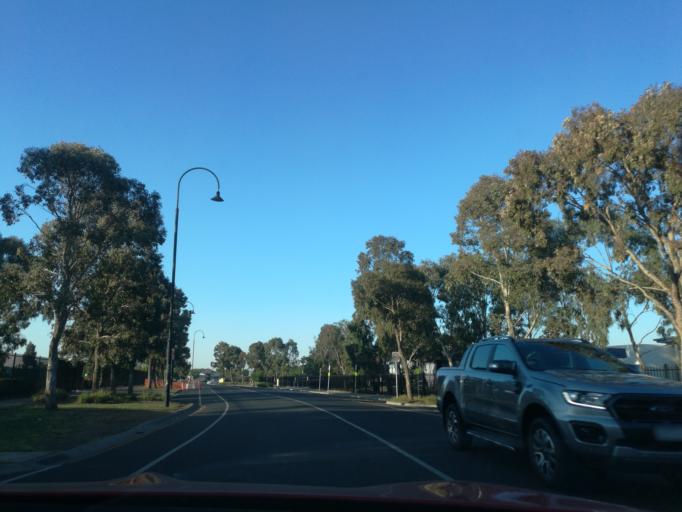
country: AU
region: Victoria
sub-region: Wyndham
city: Williams Landing
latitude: -37.8839
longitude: 144.7436
